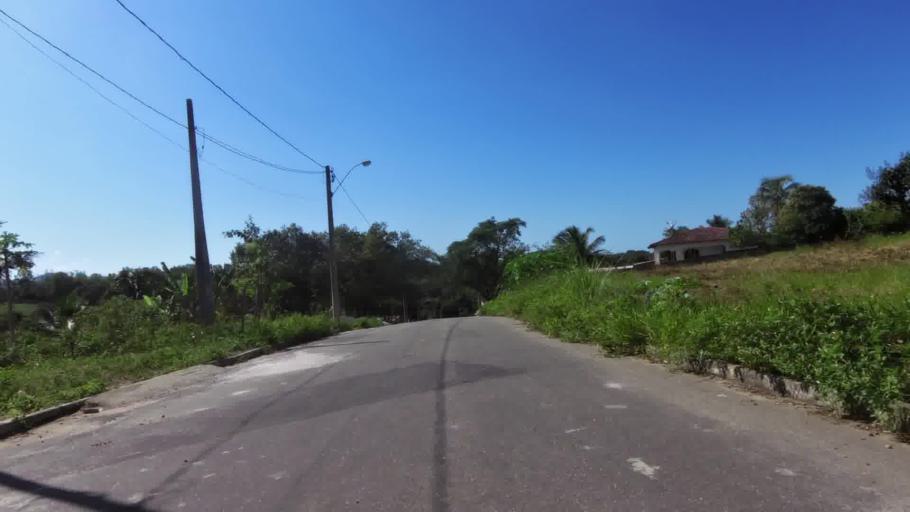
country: BR
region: Espirito Santo
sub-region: Guarapari
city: Guarapari
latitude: -20.7333
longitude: -40.5506
